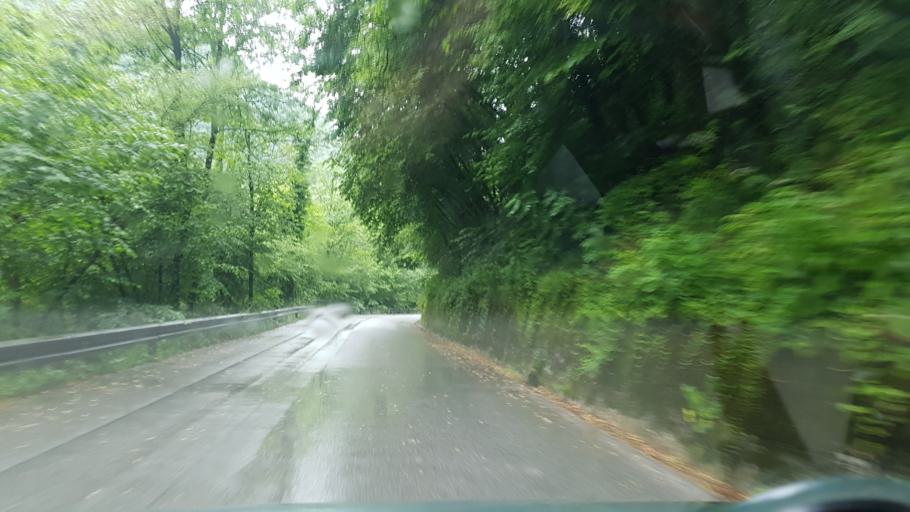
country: IT
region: Friuli Venezia Giulia
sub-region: Provincia di Udine
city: Taipana
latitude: 46.2473
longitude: 13.3094
